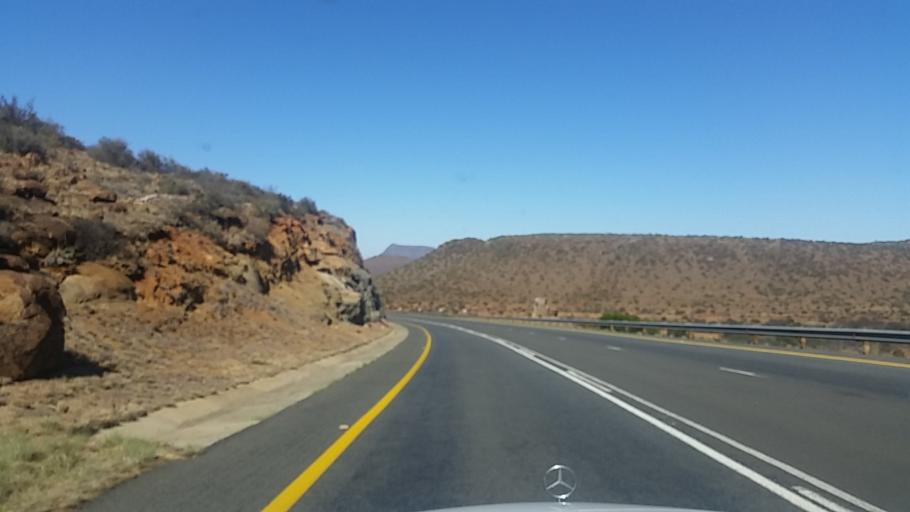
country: ZA
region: Eastern Cape
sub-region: Cacadu District Municipality
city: Graaff-Reinet
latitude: -32.0581
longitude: 24.6102
